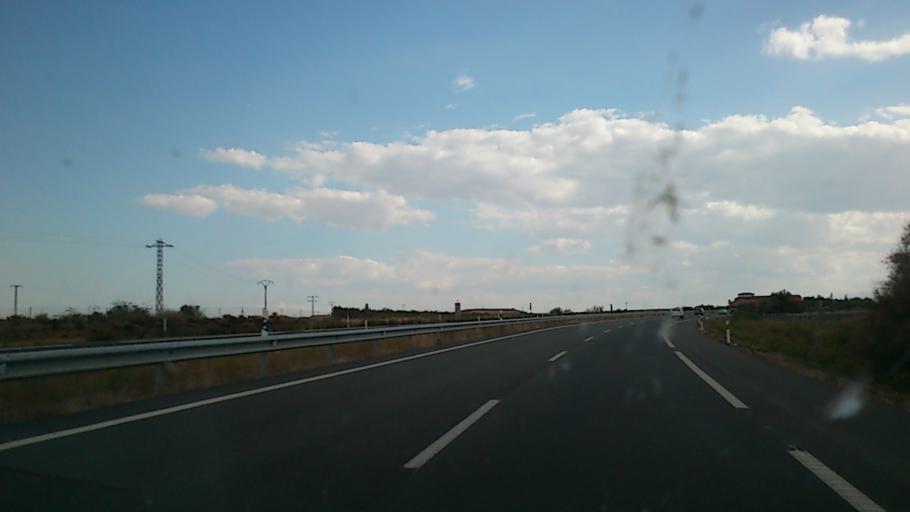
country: ES
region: La Rioja
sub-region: Provincia de La Rioja
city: Aldeanueva de Ebro
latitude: 42.2440
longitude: -1.9021
